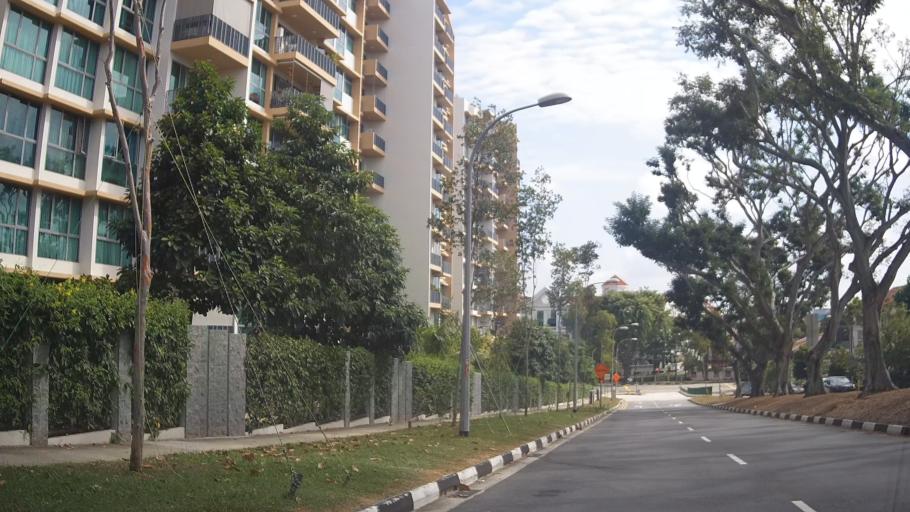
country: SG
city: Singapore
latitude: 1.3270
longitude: 103.9491
